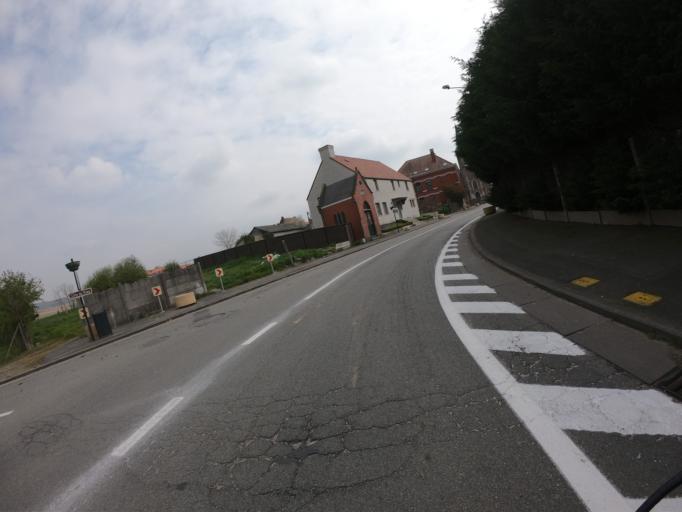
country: BE
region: Flanders
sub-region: Provincie Oost-Vlaanderen
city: Ronse
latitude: 50.7451
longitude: 3.5298
